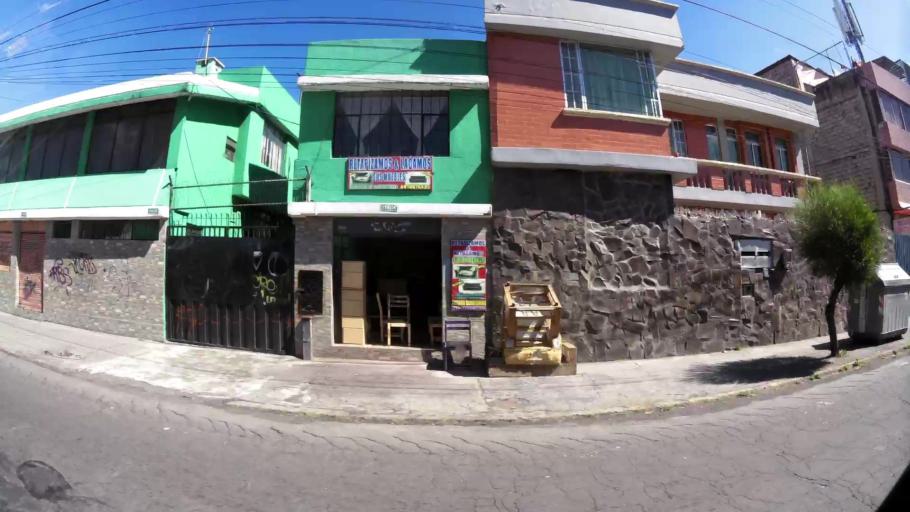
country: EC
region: Pichincha
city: Quito
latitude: -0.2636
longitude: -78.5312
